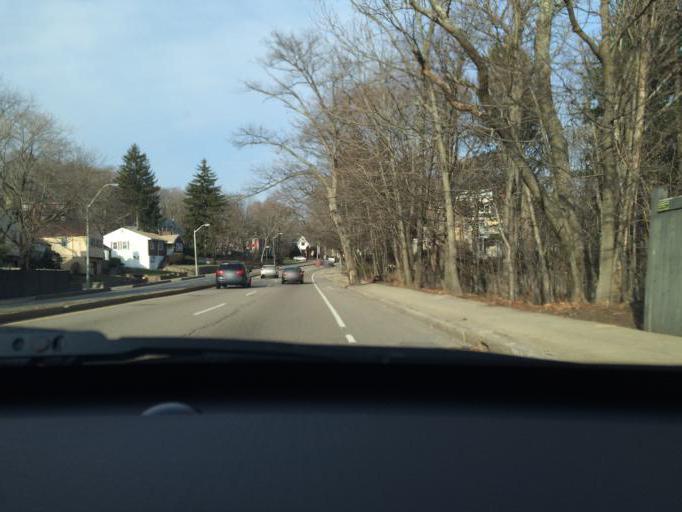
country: US
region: Massachusetts
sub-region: Suffolk County
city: Jamaica Plain
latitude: 42.3043
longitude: -71.1247
